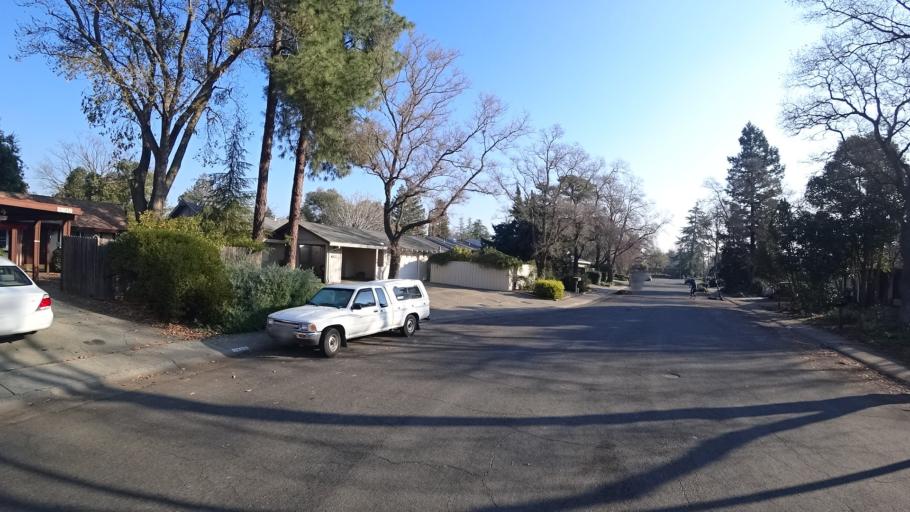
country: US
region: California
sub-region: Yolo County
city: Davis
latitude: 38.5544
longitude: -121.7931
